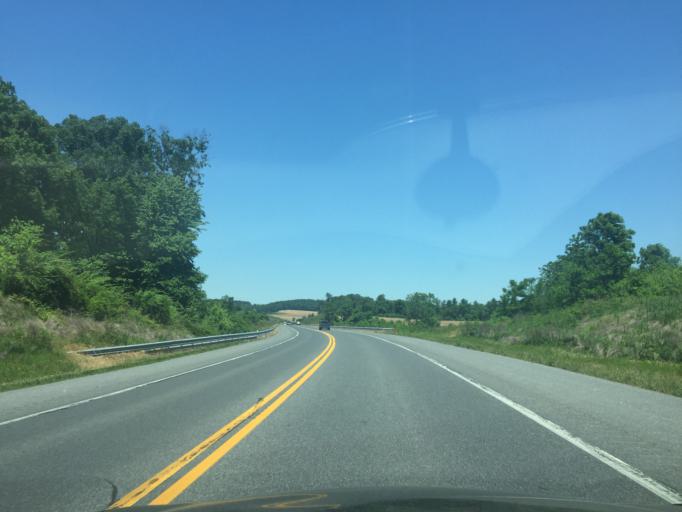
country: US
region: Maryland
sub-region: Carroll County
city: Hampstead
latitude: 39.6193
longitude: -76.8624
